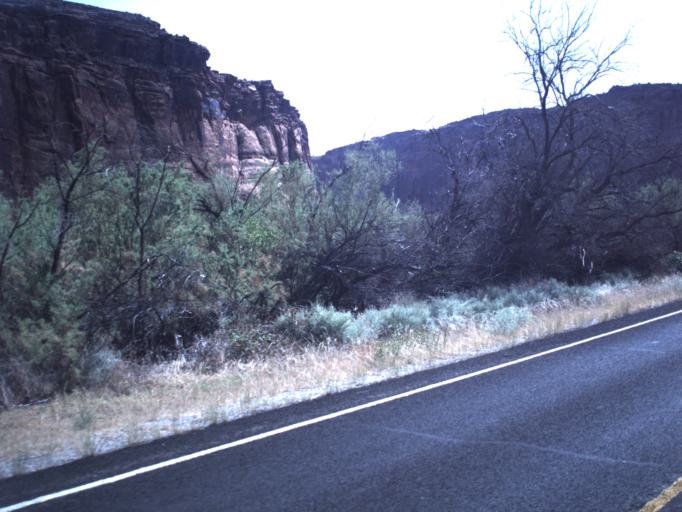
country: US
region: Utah
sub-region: Grand County
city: Moab
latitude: 38.5711
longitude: -109.6558
